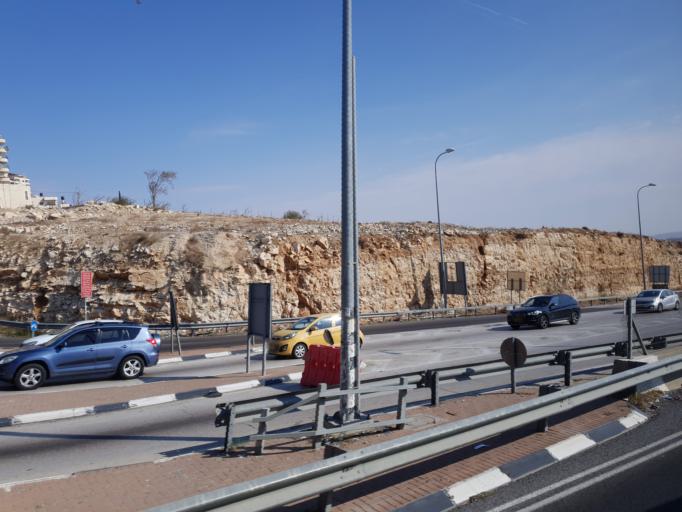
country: PS
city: Az Za`ayyim
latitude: 31.7831
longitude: 35.2638
